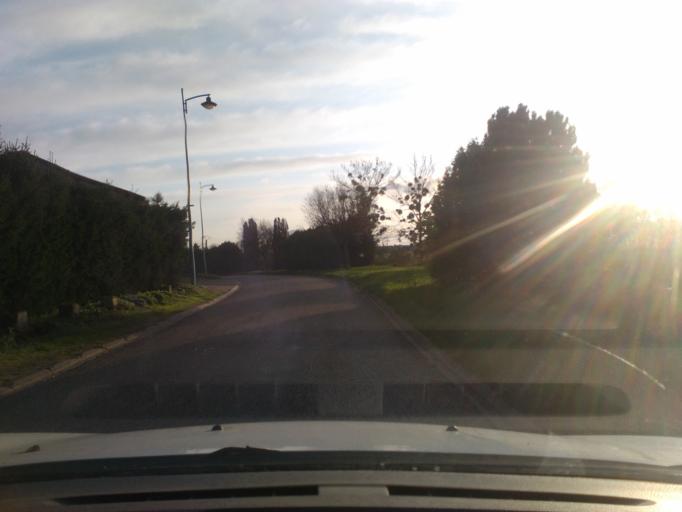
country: FR
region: Lorraine
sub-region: Departement des Vosges
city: Mirecourt
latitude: 48.2396
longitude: 6.1524
